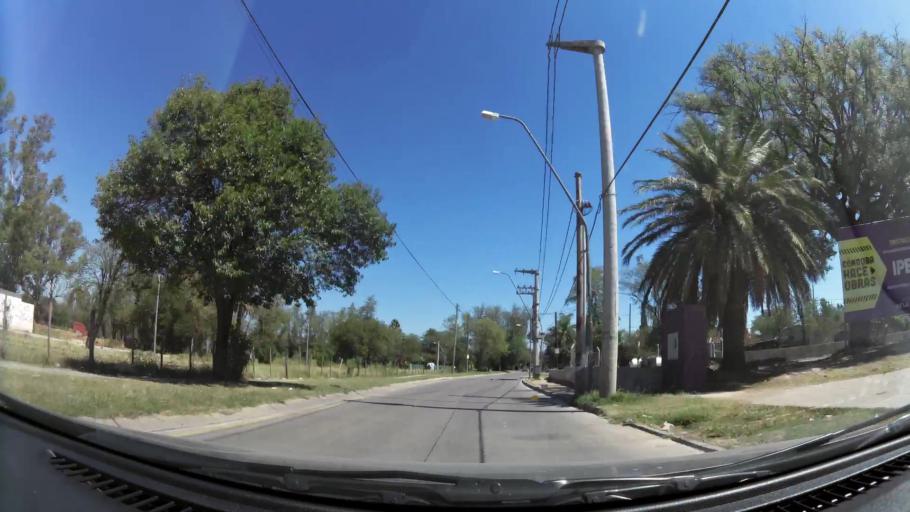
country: AR
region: Cordoba
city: Villa Allende
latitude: -31.3356
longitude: -64.2752
